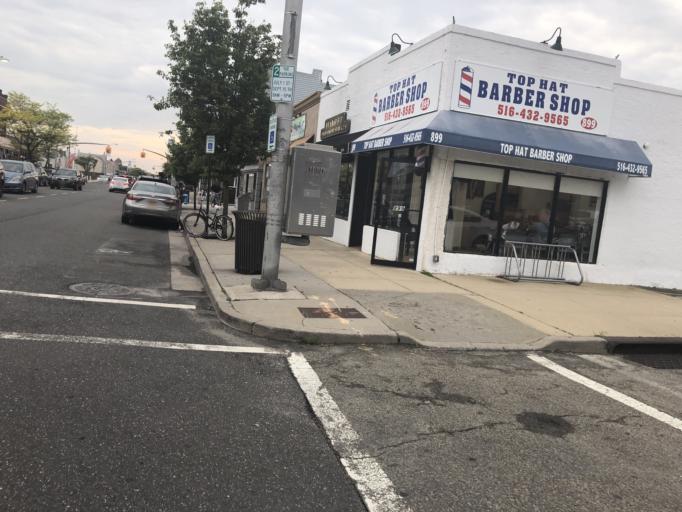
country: US
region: New York
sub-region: Nassau County
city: Harbor Isle
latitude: 40.5861
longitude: -73.6914
